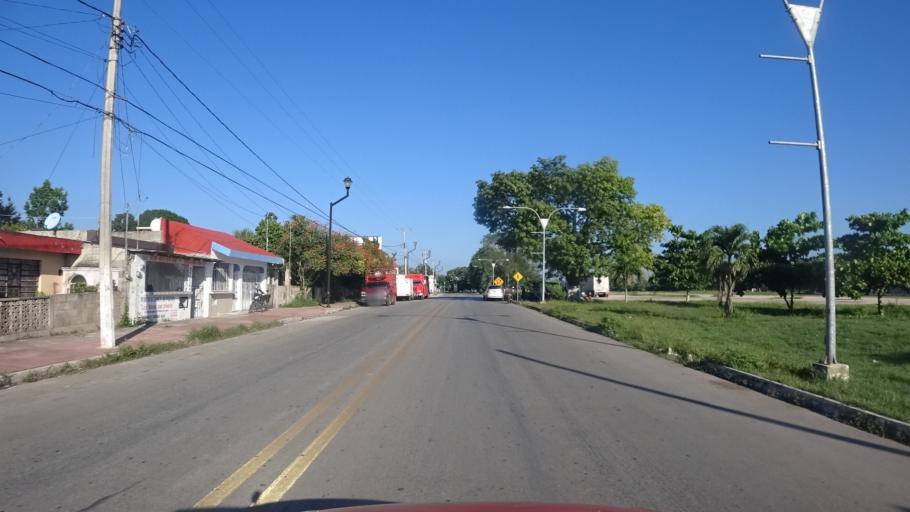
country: MX
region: Yucatan
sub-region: Tizimin
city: Tizimin
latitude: 21.1515
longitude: -88.1664
